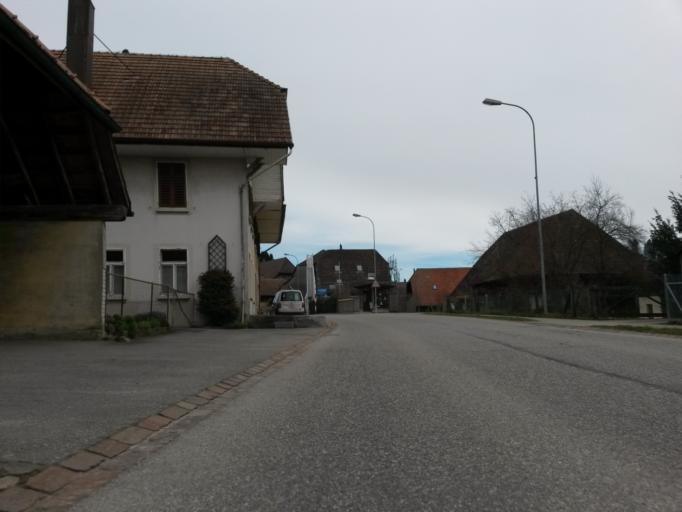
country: CH
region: Bern
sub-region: Seeland District
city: Leuzigen
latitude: 47.1750
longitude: 7.4585
